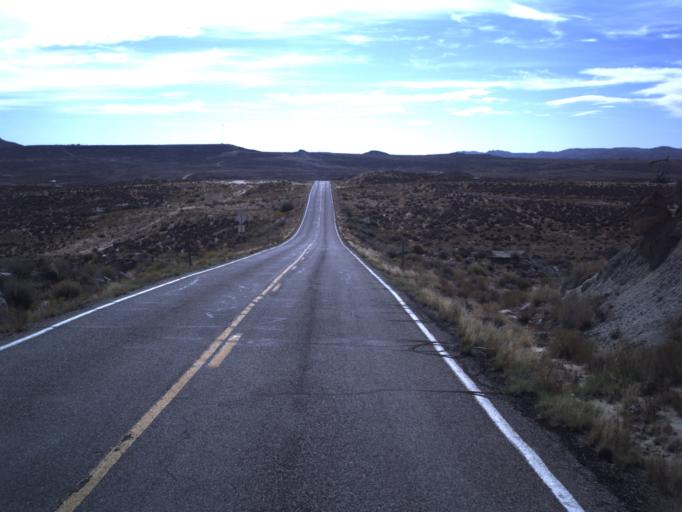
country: US
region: Utah
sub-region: San Juan County
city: Blanding
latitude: 37.3215
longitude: -109.3127
